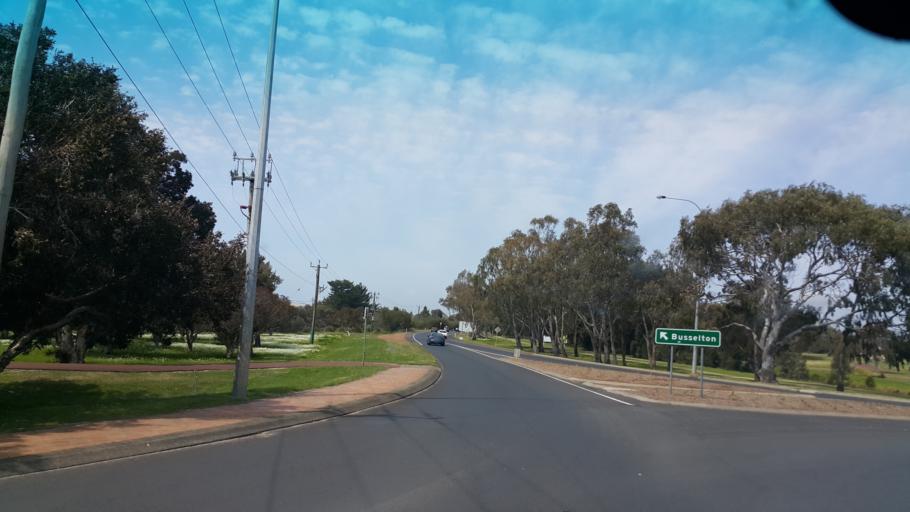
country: AU
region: Western Australia
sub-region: Busselton
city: Dunsborough
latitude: -33.6178
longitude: 115.1077
